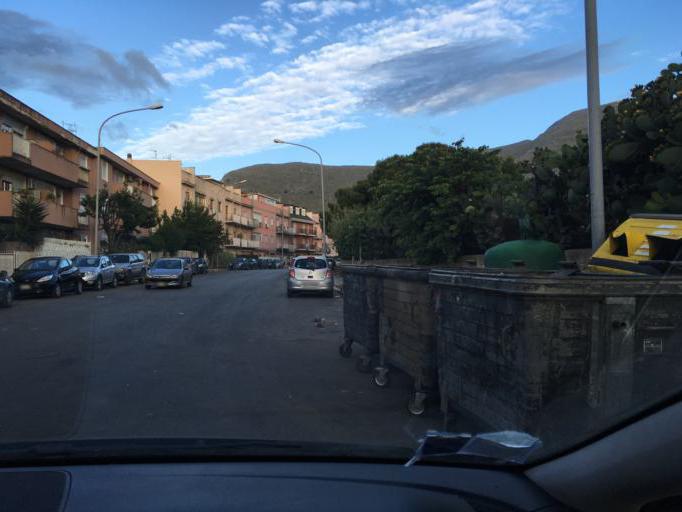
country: IT
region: Sicily
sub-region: Palermo
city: Isola delle Femmine
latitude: 38.1975
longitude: 13.3122
